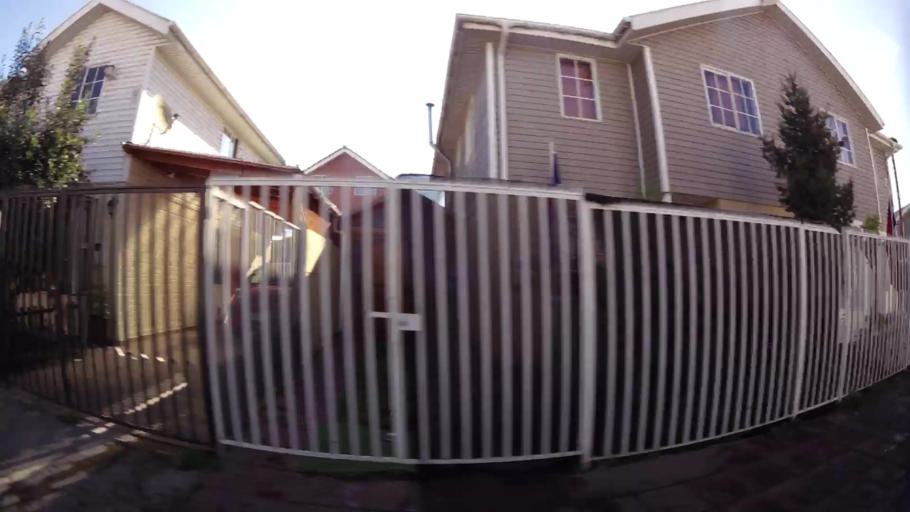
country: CL
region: Santiago Metropolitan
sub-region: Provincia de Santiago
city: Lo Prado
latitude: -33.4933
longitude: -70.7816
